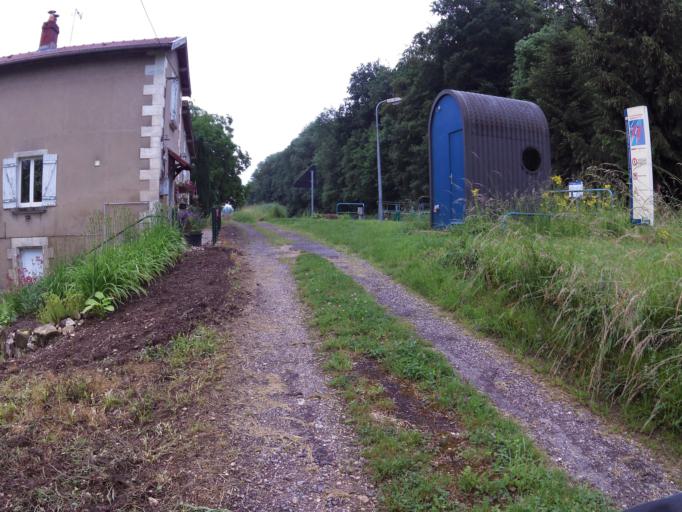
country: FR
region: Lorraine
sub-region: Departement de la Meuse
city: Fains-Veel
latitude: 48.8038
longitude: 5.1047
